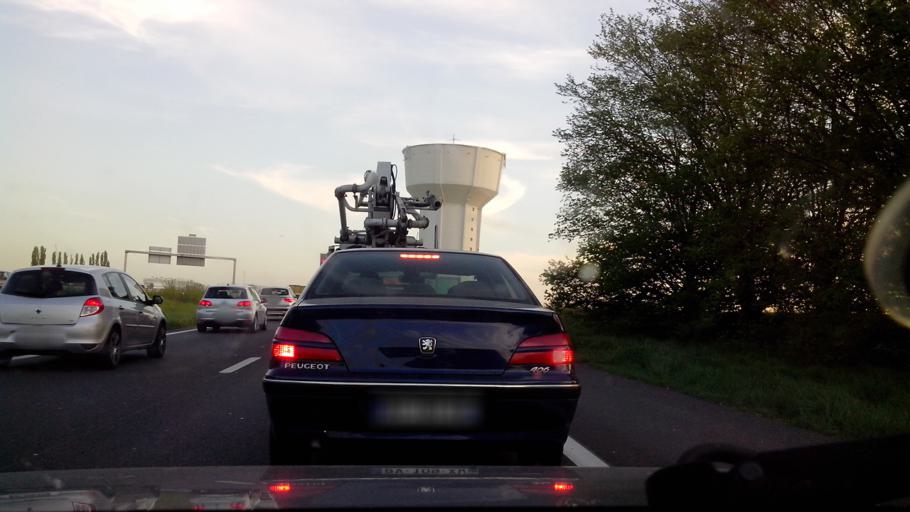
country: FR
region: Ile-de-France
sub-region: Departement de l'Essonne
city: Saclay
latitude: 48.7278
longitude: 2.1655
